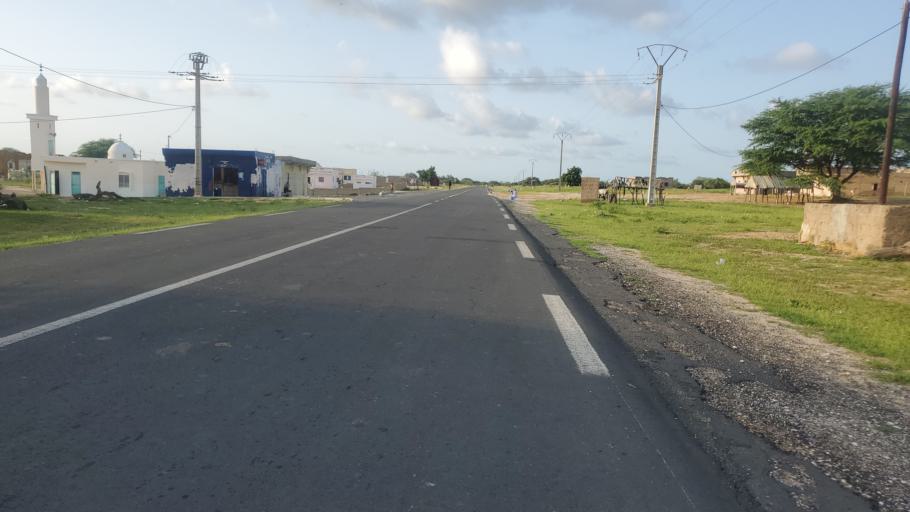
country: SN
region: Saint-Louis
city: Saint-Louis
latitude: 16.1537
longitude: -16.4098
